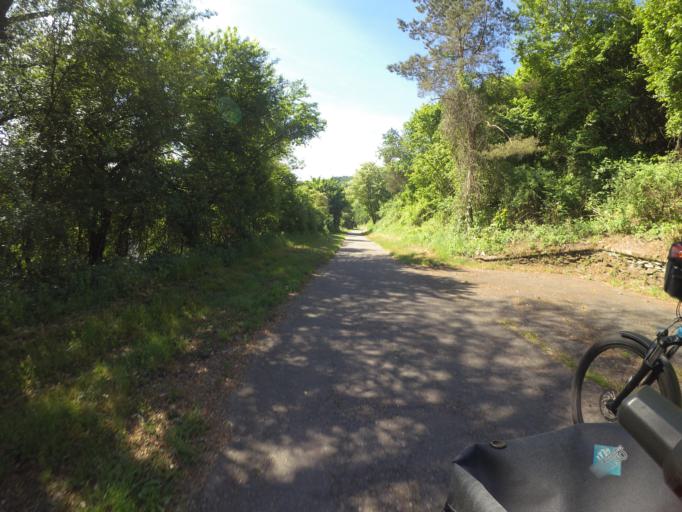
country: DE
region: Rheinland-Pfalz
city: Kanzem
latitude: 49.6677
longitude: 6.5551
